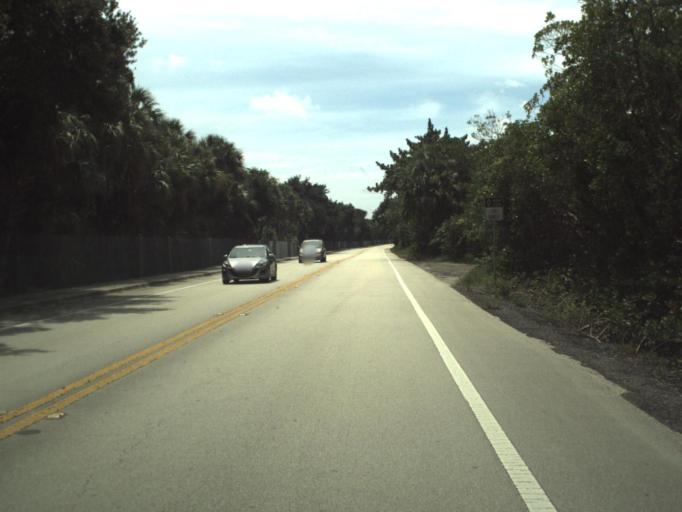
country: US
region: Florida
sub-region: Palm Beach County
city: Lake Park
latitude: 26.8295
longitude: -80.0468
